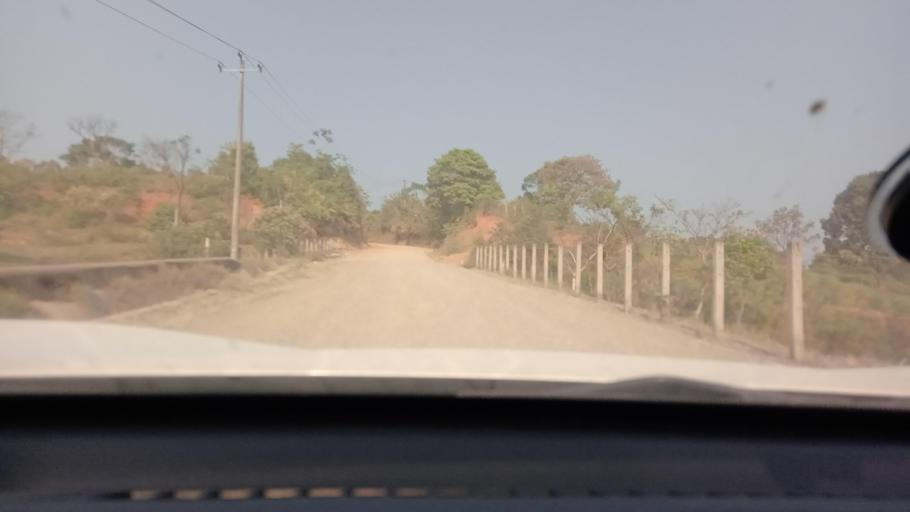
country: MX
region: Tabasco
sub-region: Huimanguillo
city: Francisco Rueda
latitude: 17.6527
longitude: -93.8860
